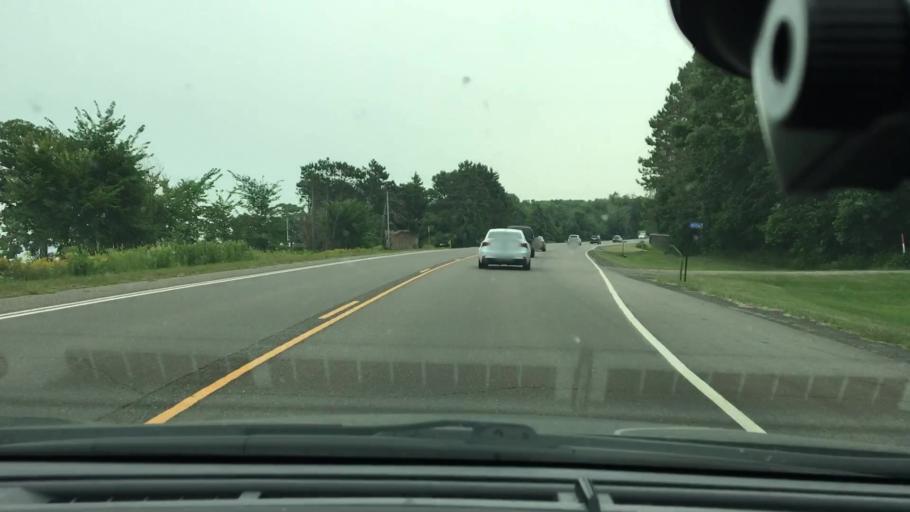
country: US
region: Minnesota
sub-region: Mille Lacs County
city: Vineland
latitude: 46.1349
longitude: -93.6927
